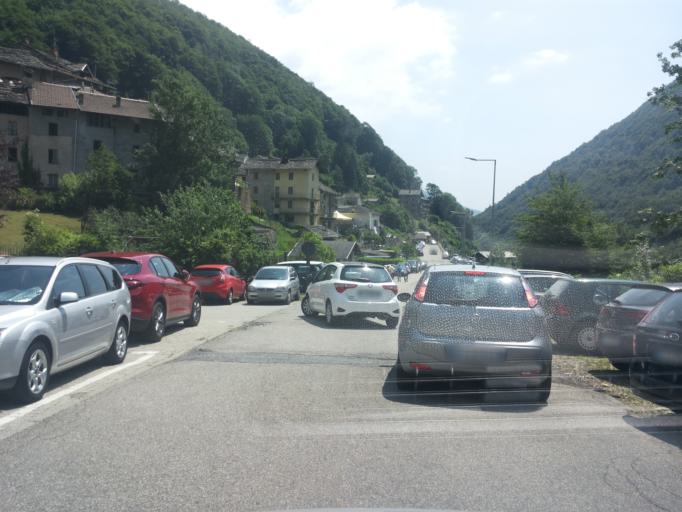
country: IT
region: Piedmont
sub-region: Provincia di Biella
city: Piedicavallo
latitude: 45.6886
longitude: 7.9557
